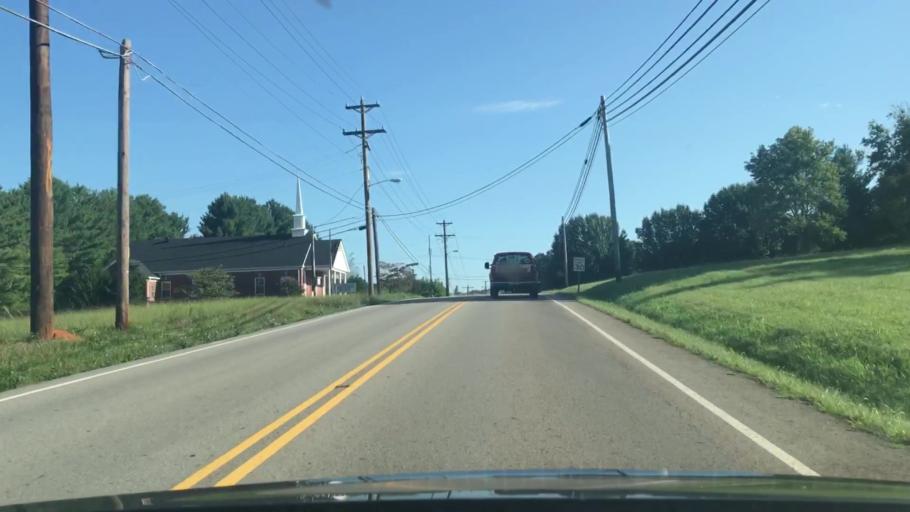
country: US
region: Tennessee
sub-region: Overton County
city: Livingston
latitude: 36.3907
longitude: -85.3039
